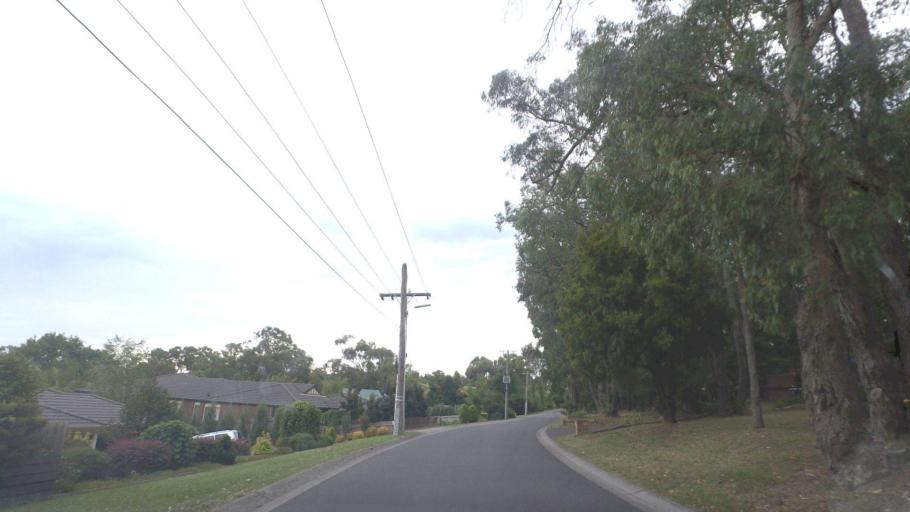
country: AU
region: Victoria
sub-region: Yarra Ranges
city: Mount Evelyn
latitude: -37.7669
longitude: 145.3754
